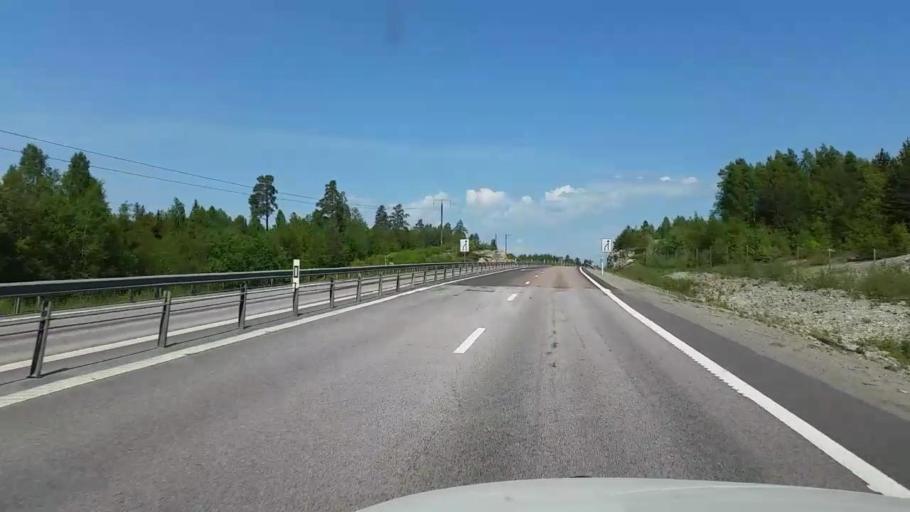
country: SE
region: Gaevleborg
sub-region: Hudiksvalls Kommun
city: Hudiksvall
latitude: 61.7301
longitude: 17.0656
